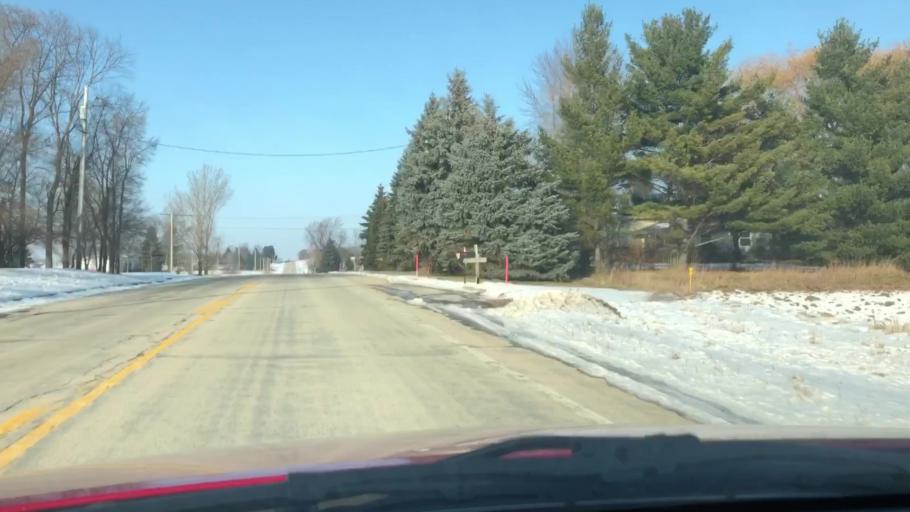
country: US
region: Wisconsin
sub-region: Outagamie County
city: Kimberly
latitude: 44.3686
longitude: -88.3748
